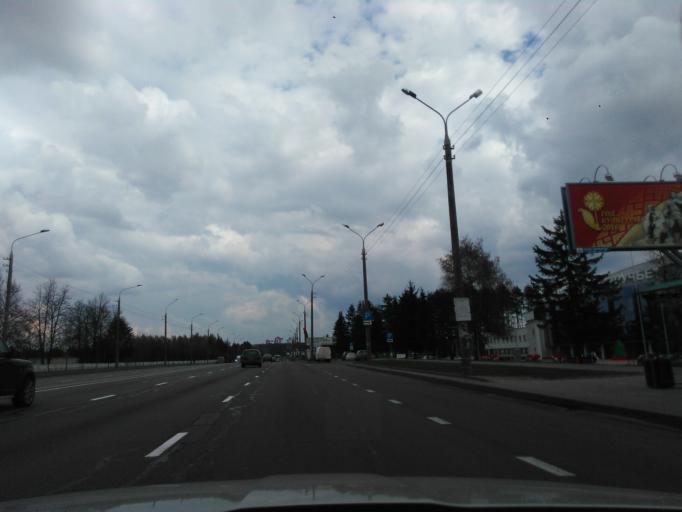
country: BY
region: Minsk
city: Lyeskawka
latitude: 53.9510
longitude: 27.7064
